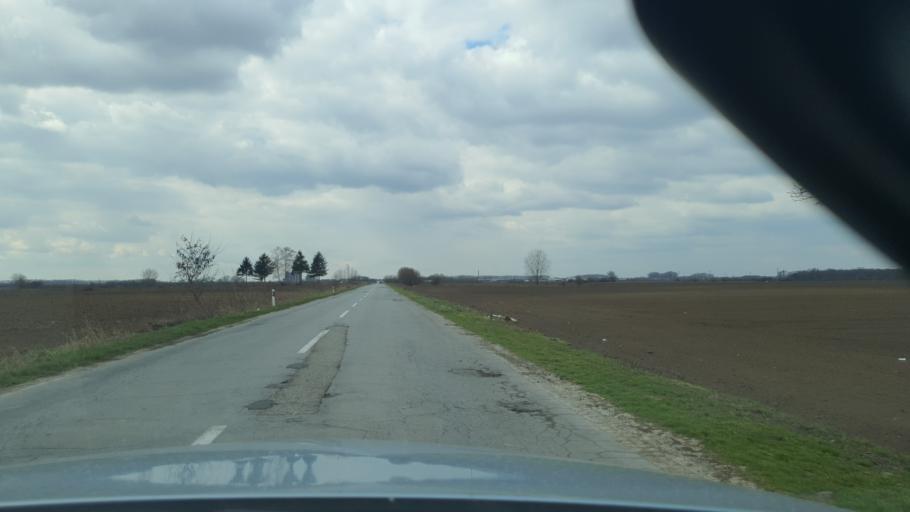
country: RS
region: Autonomna Pokrajina Vojvodina
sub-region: Juznobacki Okrug
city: Bac
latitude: 45.3991
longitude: 19.2728
